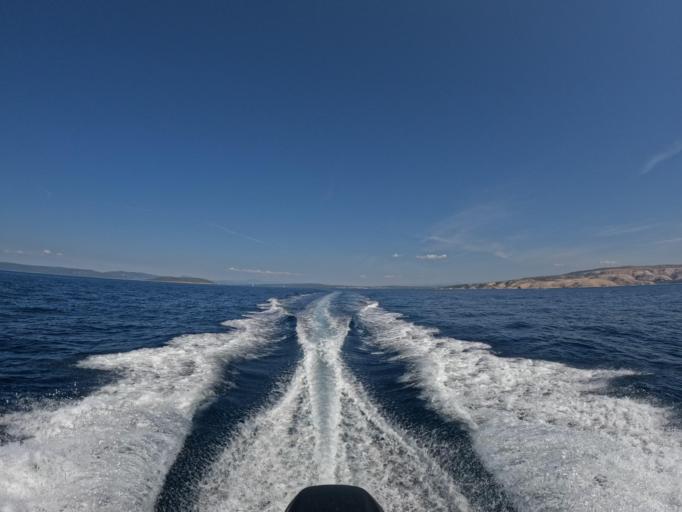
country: HR
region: Primorsko-Goranska
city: Punat
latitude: 44.9171
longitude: 14.6243
